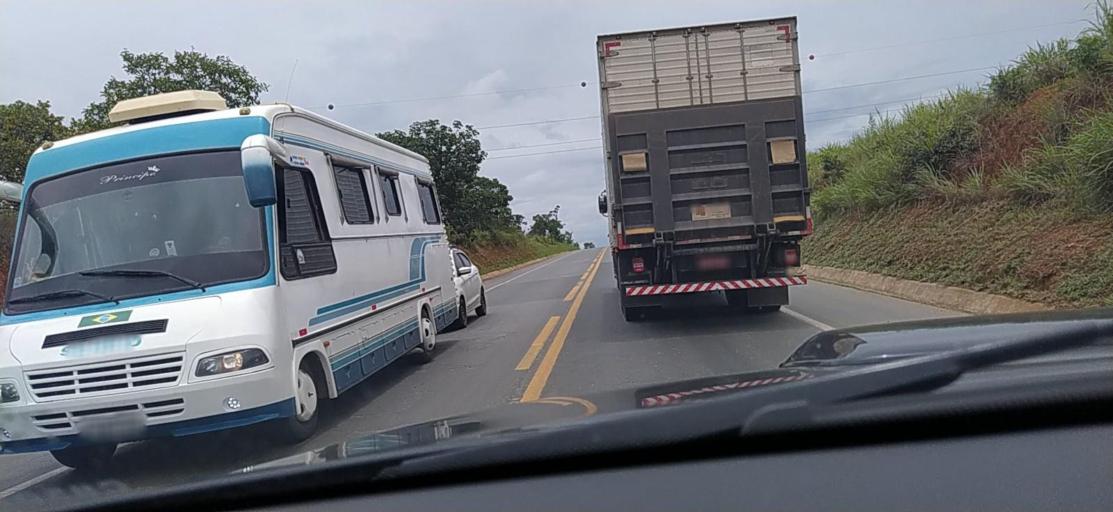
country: BR
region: Minas Gerais
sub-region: Curvelo
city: Curvelo
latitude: -18.7325
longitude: -44.4427
